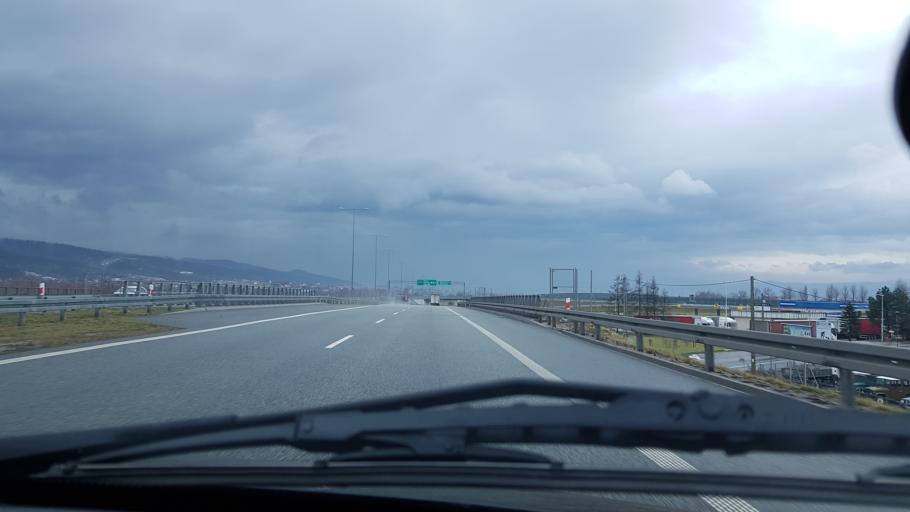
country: PL
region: Silesian Voivodeship
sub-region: Powiat bielski
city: Rybarzowice
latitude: 49.7410
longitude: 19.1007
